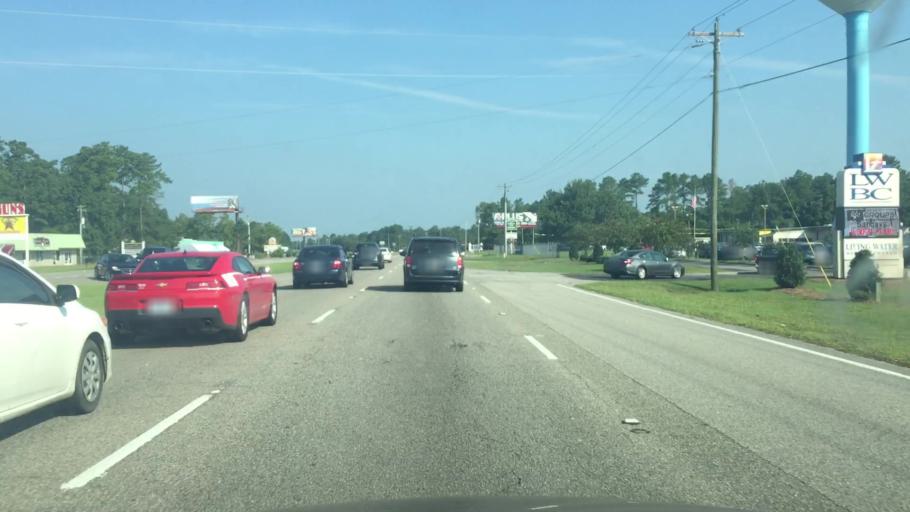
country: US
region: South Carolina
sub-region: Horry County
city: North Myrtle Beach
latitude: 33.9012
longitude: -78.7000
